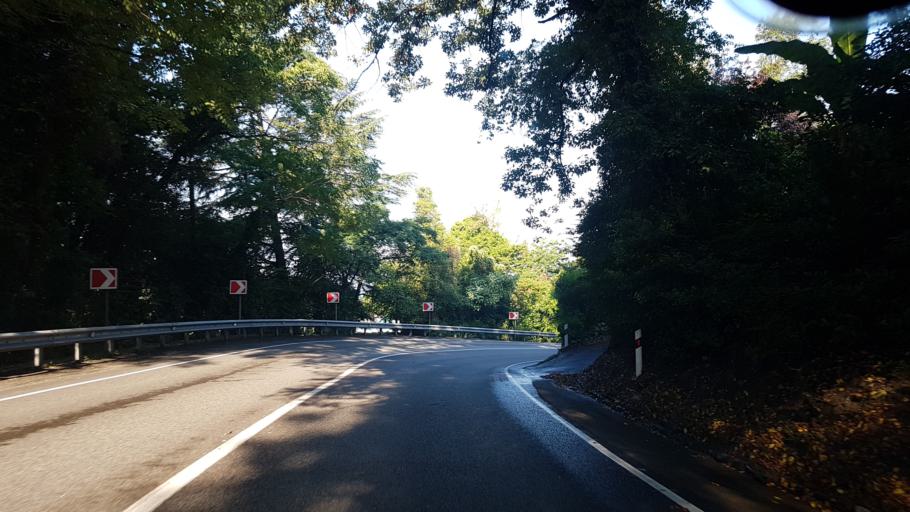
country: RU
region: Krasnodarskiy
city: Vardane
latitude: 43.7917
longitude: 39.4801
